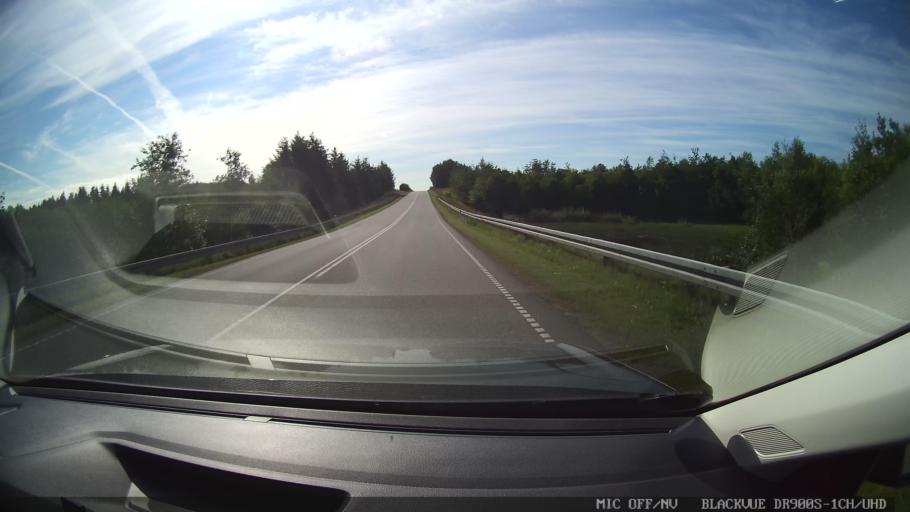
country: DK
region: North Denmark
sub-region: Mariagerfjord Kommune
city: Hadsund
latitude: 56.7681
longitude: 10.0627
